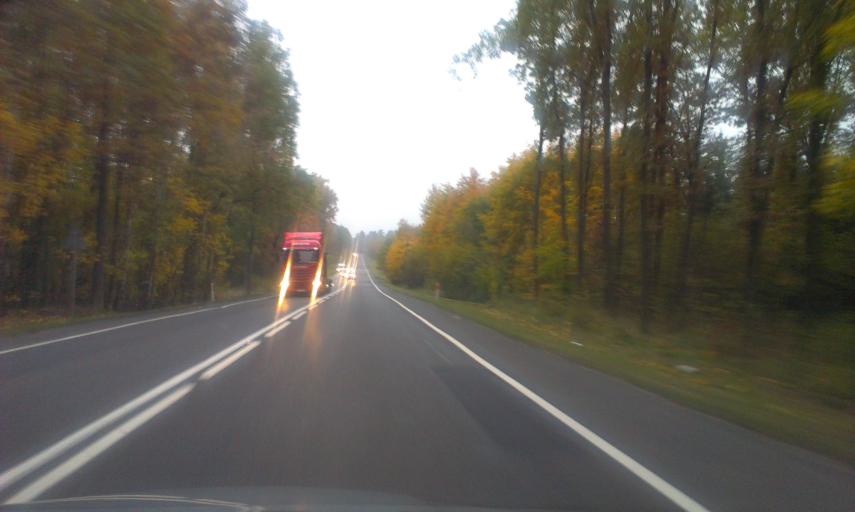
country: PL
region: Greater Poland Voivodeship
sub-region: Powiat chodzieski
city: Budzyn
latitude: 52.9273
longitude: 16.9666
